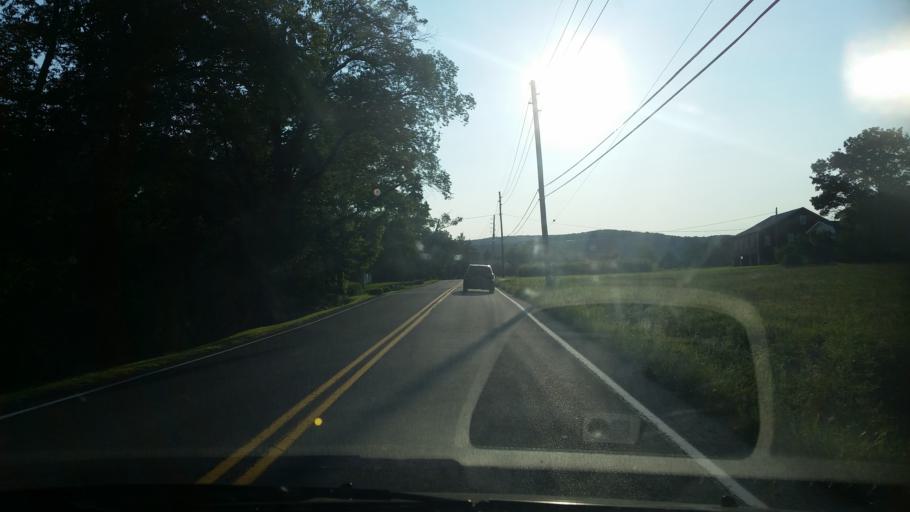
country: US
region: Pennsylvania
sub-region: Blair County
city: Greenwood
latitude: 40.5769
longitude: -78.3619
